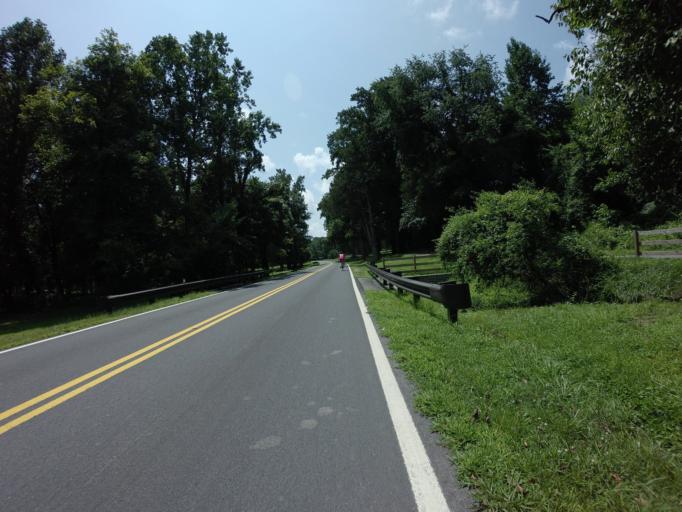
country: US
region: Maryland
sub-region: Montgomery County
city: Forest Glen
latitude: 39.0116
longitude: -77.0680
